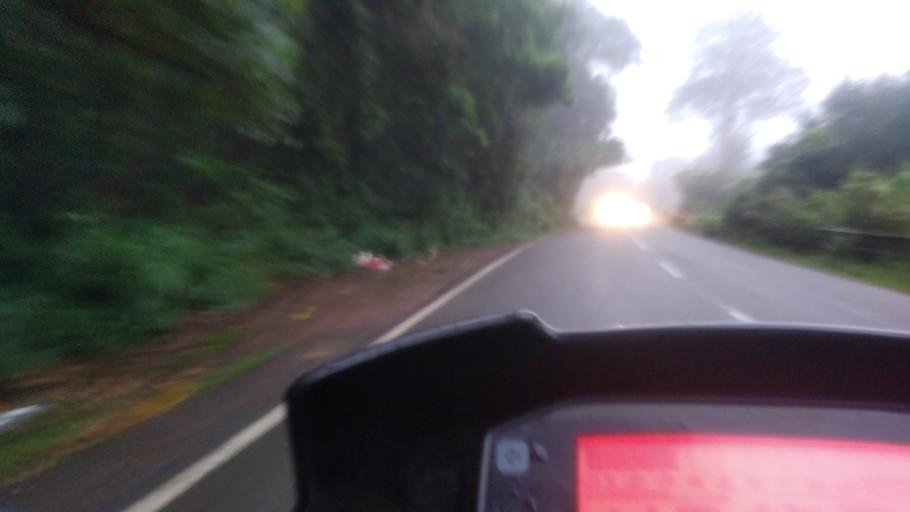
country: IN
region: Kerala
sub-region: Kottayam
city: Erattupetta
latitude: 9.5805
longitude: 76.9781
